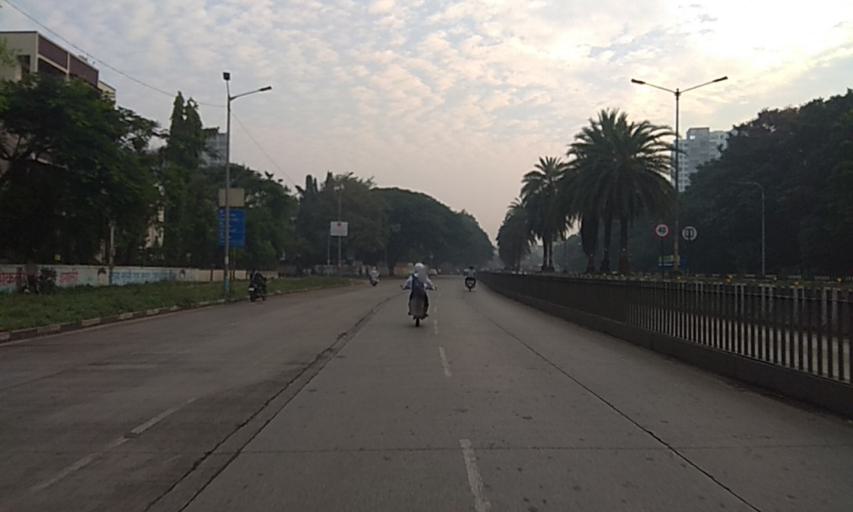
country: IN
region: Maharashtra
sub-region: Pune Division
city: Khadki
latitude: 18.5498
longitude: 73.8933
